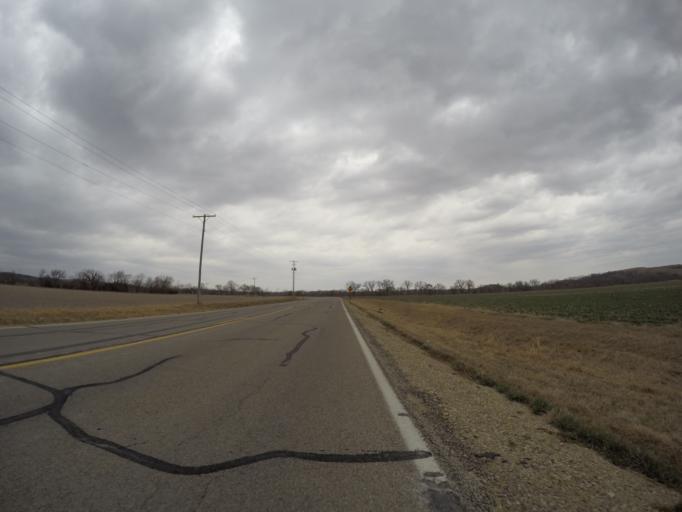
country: US
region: Kansas
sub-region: Riley County
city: Manhattan
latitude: 39.2343
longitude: -96.5680
